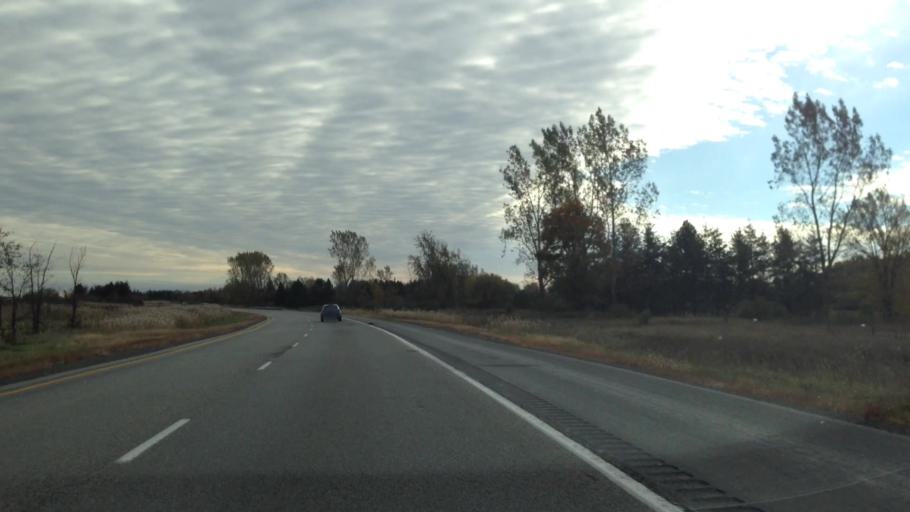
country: CA
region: Ontario
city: Casselman
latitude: 45.3026
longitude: -75.0966
